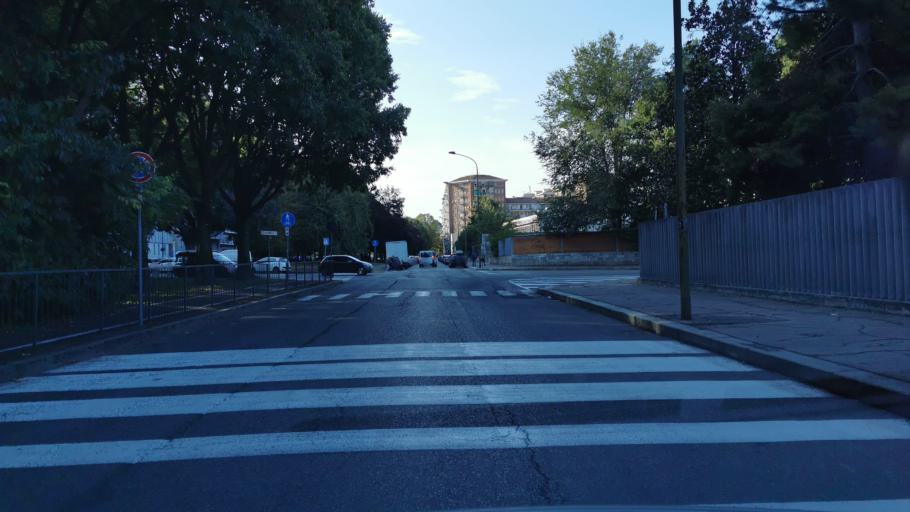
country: IT
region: Piedmont
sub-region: Provincia di Torino
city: Turin
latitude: 45.0993
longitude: 7.7051
